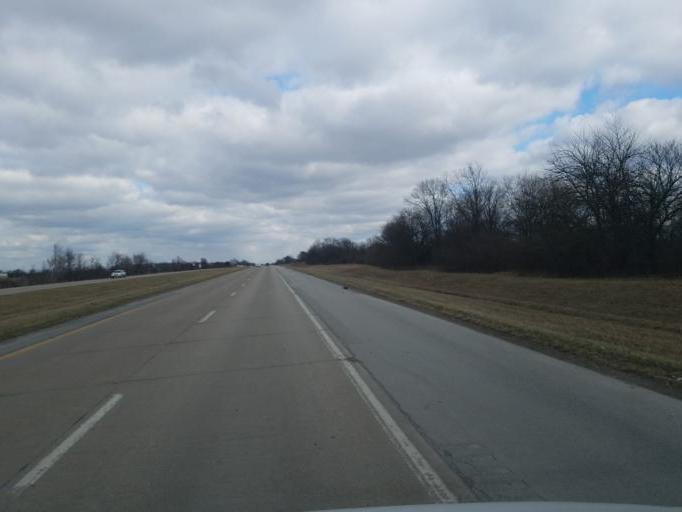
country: US
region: Indiana
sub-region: Hendricks County
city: Danville
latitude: 39.7568
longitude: -86.4829
